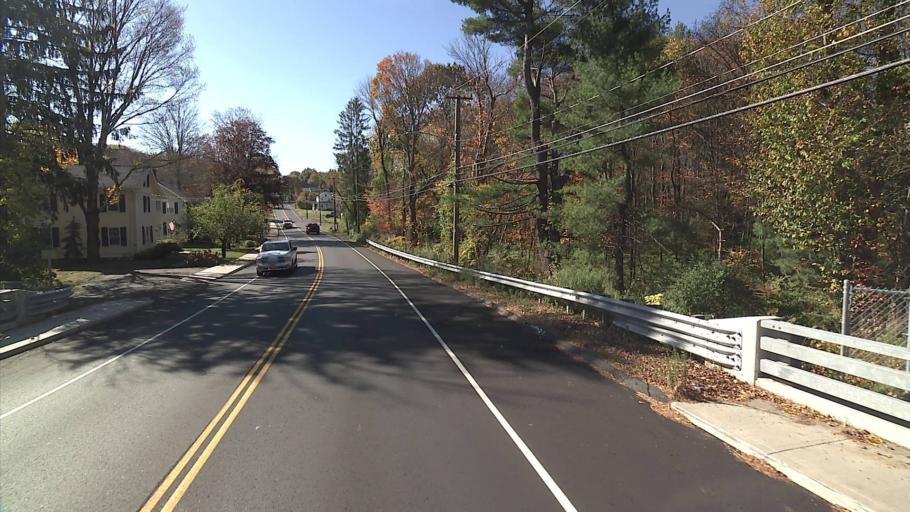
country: US
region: Connecticut
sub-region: Litchfield County
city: Watertown
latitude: 41.6103
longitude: -73.1153
